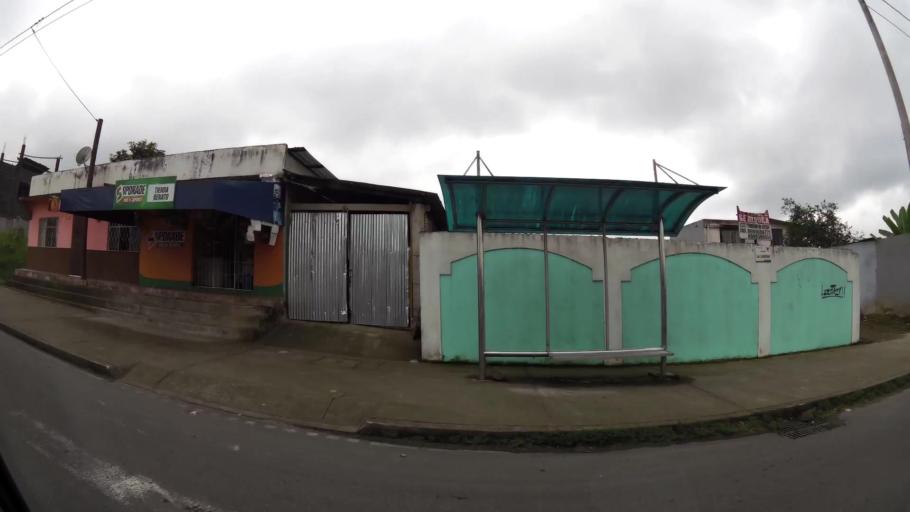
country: EC
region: Santo Domingo de los Tsachilas
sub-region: Canton Santo Domingo de los Colorados
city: Santo Domingo de los Colorados
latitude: -0.2584
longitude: -79.1454
